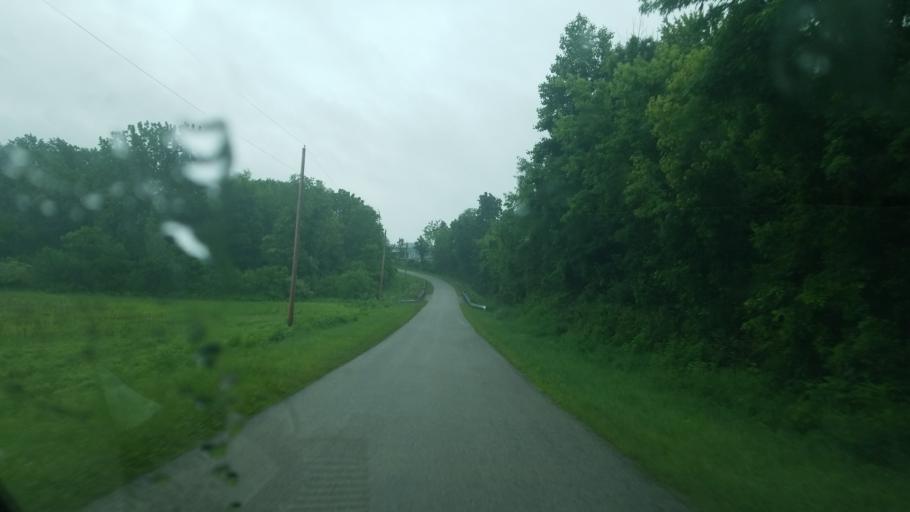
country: US
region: Ohio
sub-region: Huron County
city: Willard
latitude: 40.9444
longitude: -82.7852
